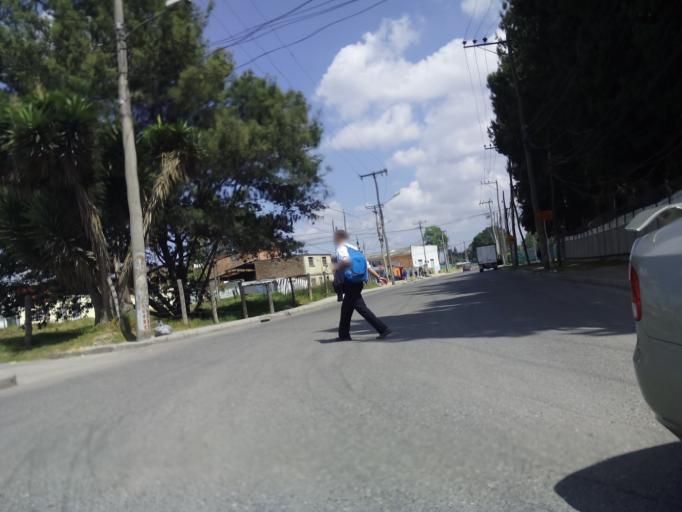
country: CO
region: Bogota D.C.
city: Bogota
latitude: 4.6820
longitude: -74.1265
